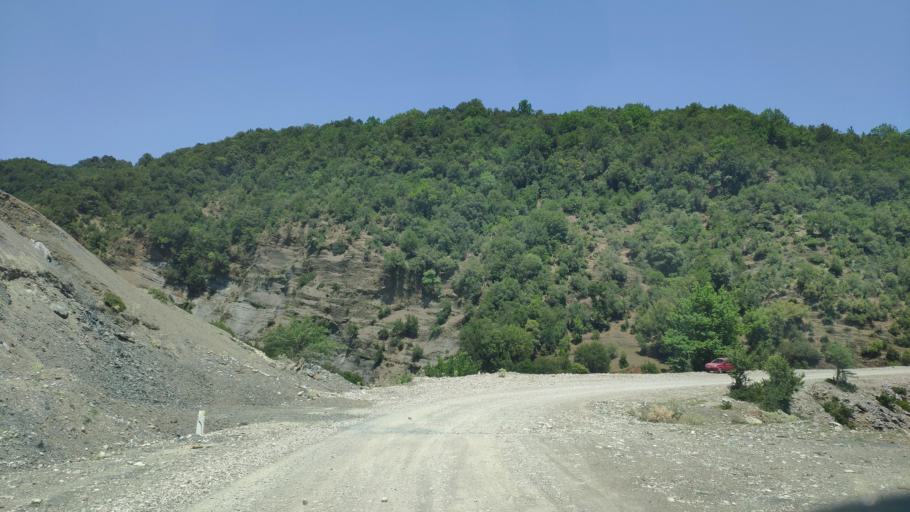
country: GR
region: Thessaly
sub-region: Nomos Kardhitsas
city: Anthiro
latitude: 39.1672
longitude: 21.3698
